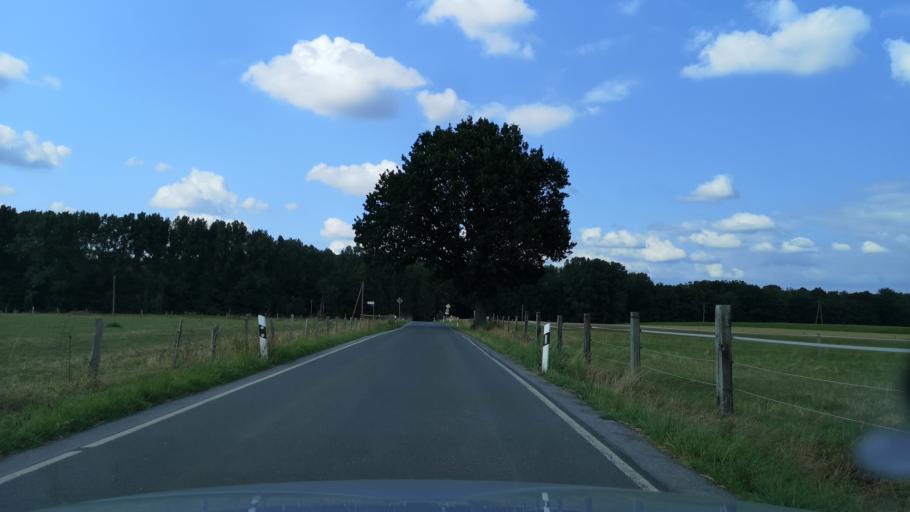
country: DE
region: North Rhine-Westphalia
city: Iserlohn
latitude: 51.4375
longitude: 7.7097
